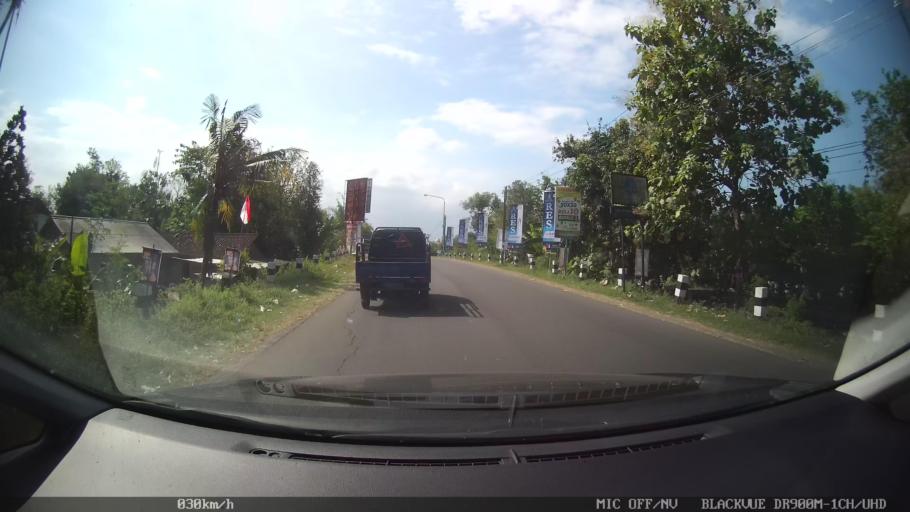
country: ID
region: Daerah Istimewa Yogyakarta
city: Sewon
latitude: -7.9050
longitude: 110.3840
